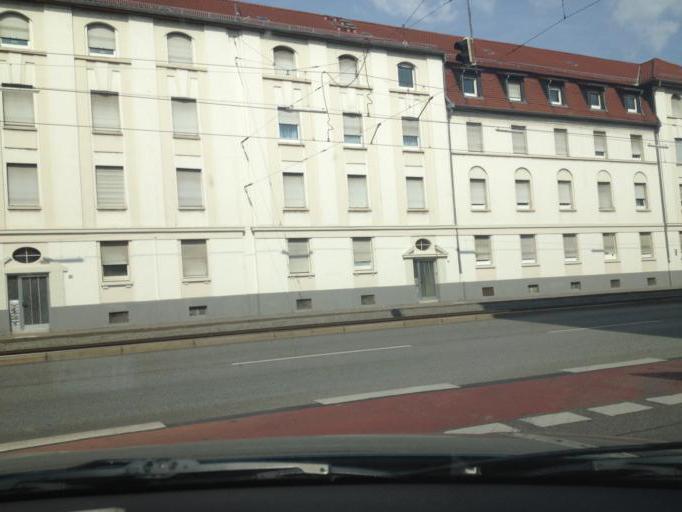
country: DE
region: Rheinland-Pfalz
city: Altrip
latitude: 49.4588
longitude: 8.4920
